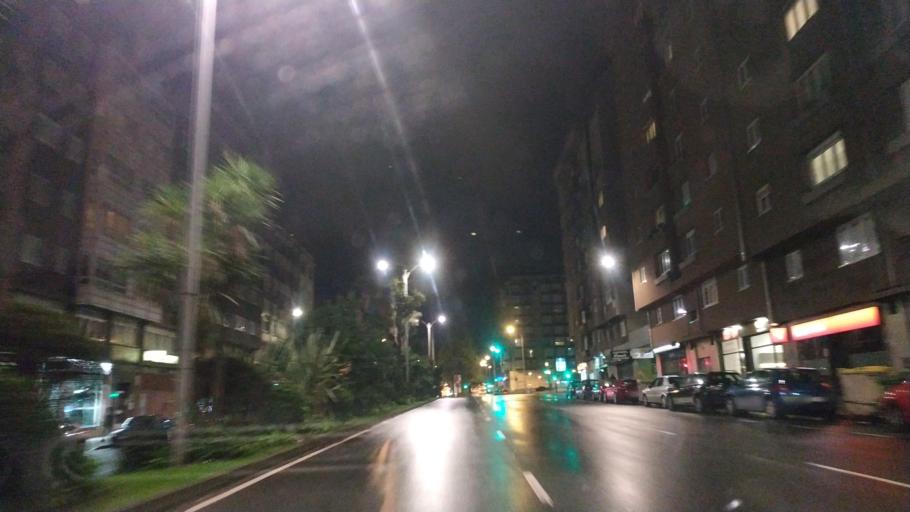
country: ES
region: Galicia
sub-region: Provincia da Coruna
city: A Coruna
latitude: 43.3568
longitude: -8.4131
